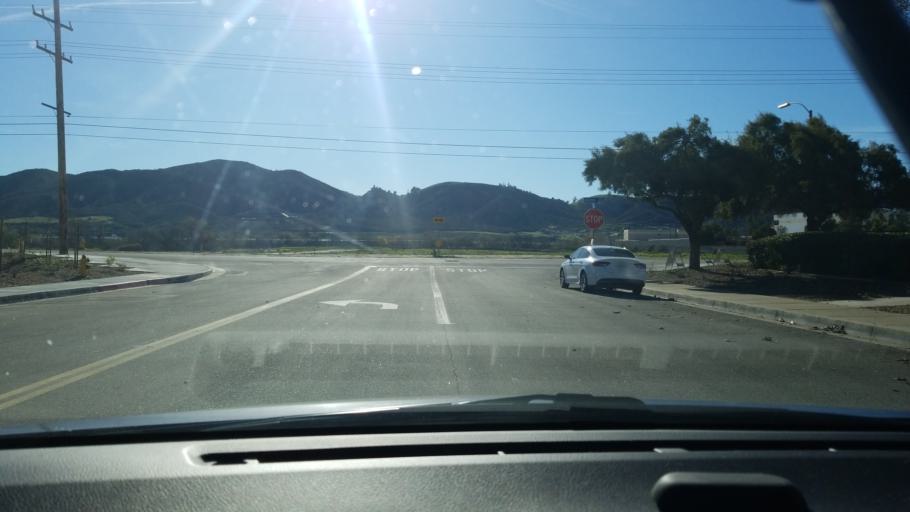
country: US
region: California
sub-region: Riverside County
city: Murrieta Hot Springs
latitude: 33.5305
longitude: -117.1822
